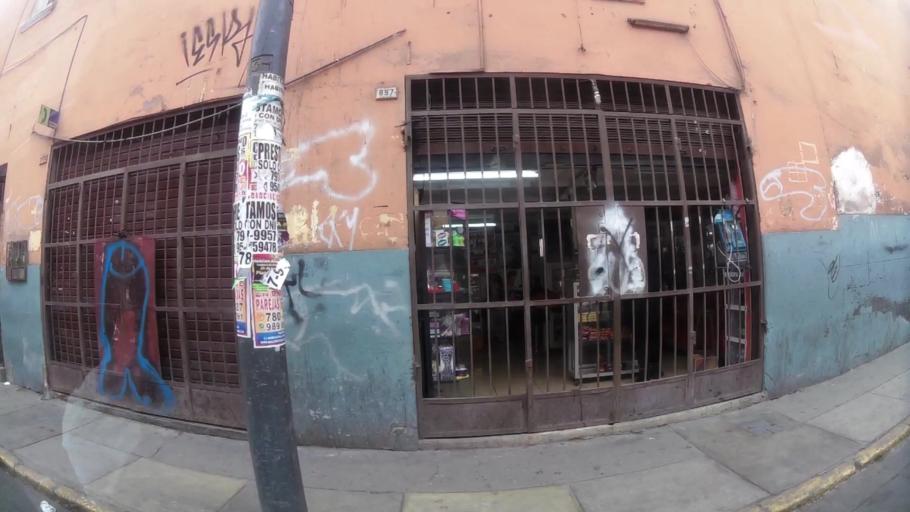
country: PE
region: Lima
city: Lima
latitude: -12.0500
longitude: -77.0230
